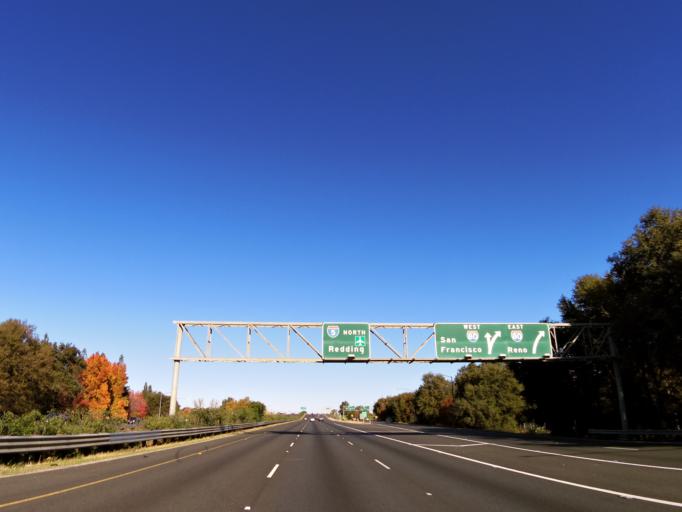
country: US
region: California
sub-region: Yolo County
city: West Sacramento
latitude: 38.6193
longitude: -121.5145
